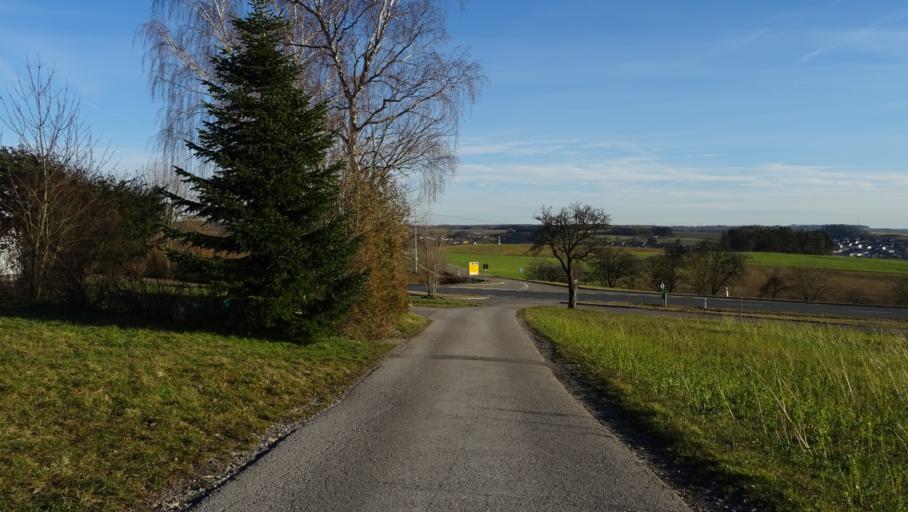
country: DE
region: Baden-Wuerttemberg
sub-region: Karlsruhe Region
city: Billigheim
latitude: 49.4091
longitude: 9.2645
